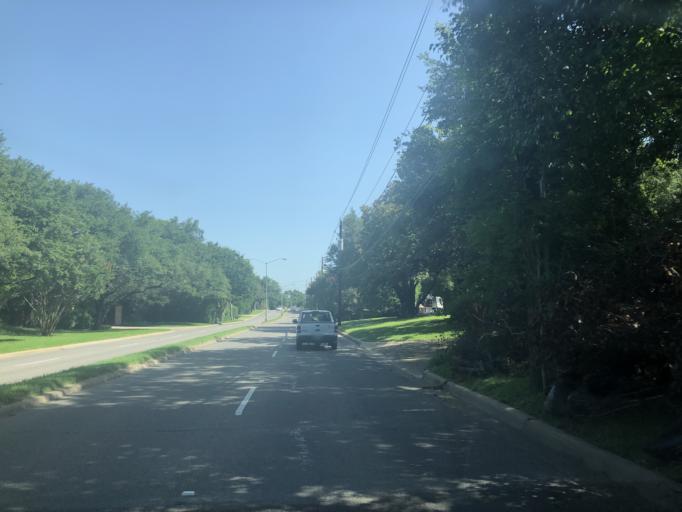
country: US
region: Texas
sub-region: Dallas County
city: University Park
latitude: 32.8835
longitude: -96.8210
